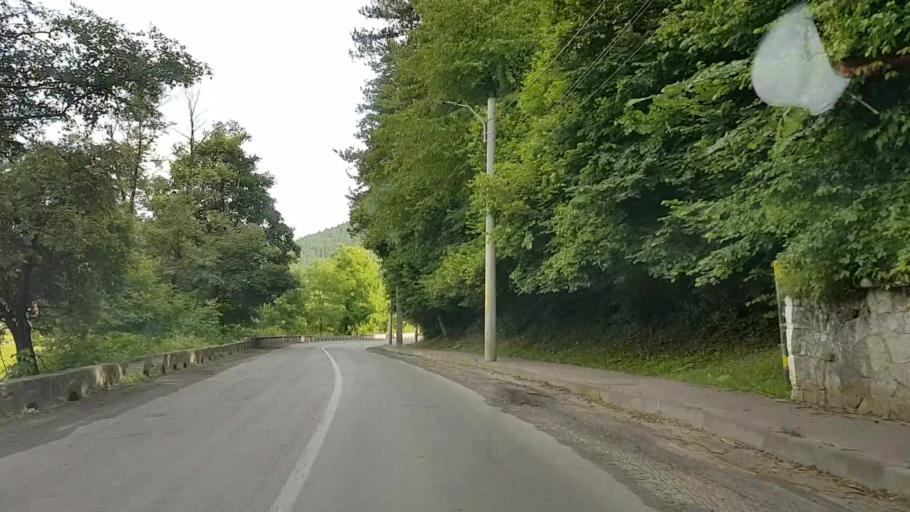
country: RO
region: Neamt
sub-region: Comuna Bicaz
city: Dodeni
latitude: 46.9170
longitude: 26.0847
